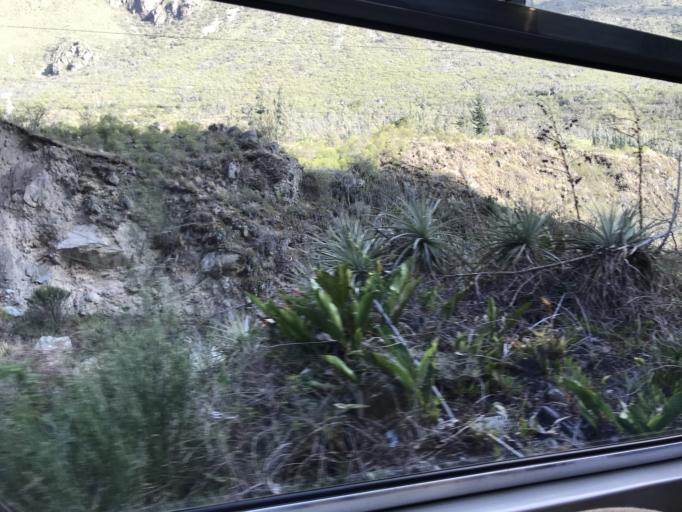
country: PE
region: Cusco
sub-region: Provincia de Urubamba
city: Ollantaytambo
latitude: -13.2221
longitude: -72.3952
